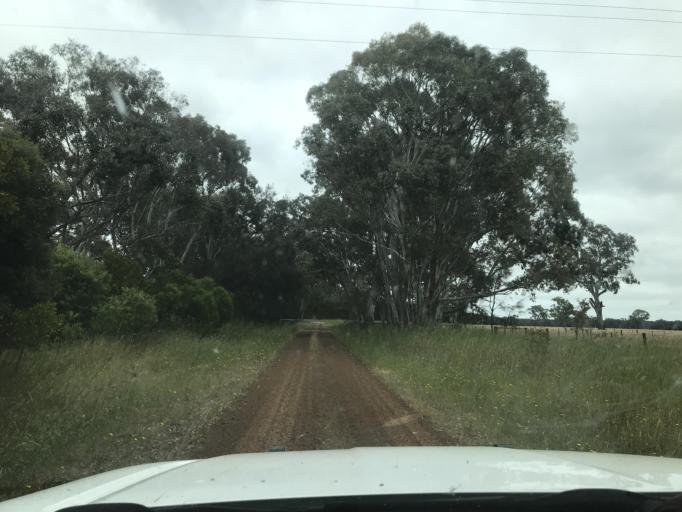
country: AU
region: South Australia
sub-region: Wattle Range
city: Penola
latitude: -37.1169
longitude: 141.0394
